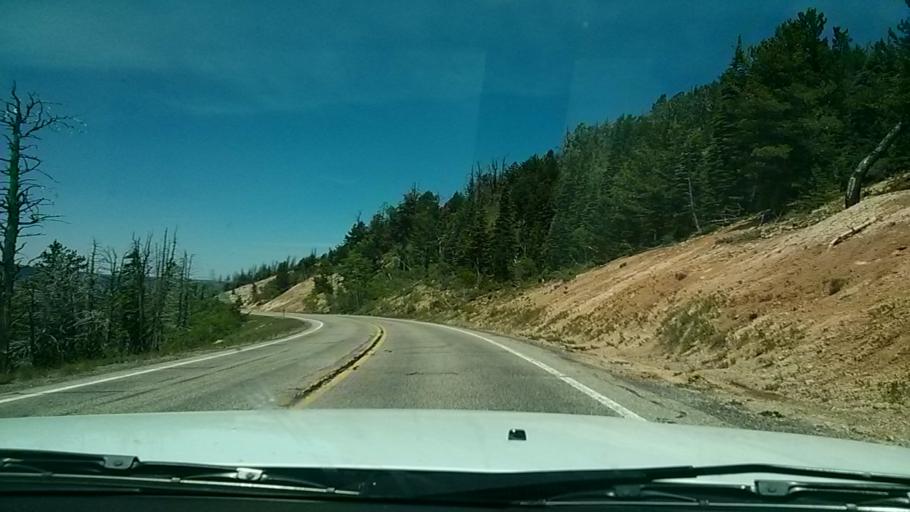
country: US
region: Utah
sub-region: Iron County
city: Cedar City
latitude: 37.5682
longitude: -112.8502
